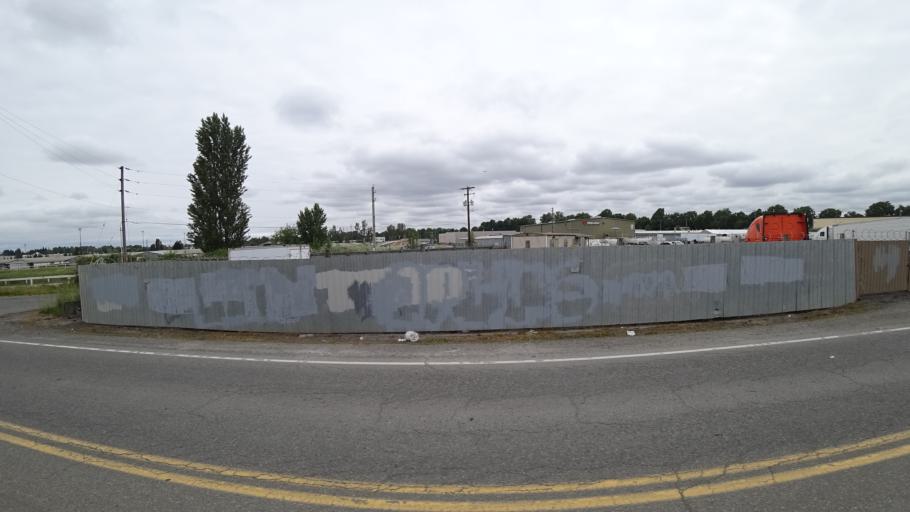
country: US
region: Washington
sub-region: Clark County
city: Vancouver
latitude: 45.5877
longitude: -122.6695
